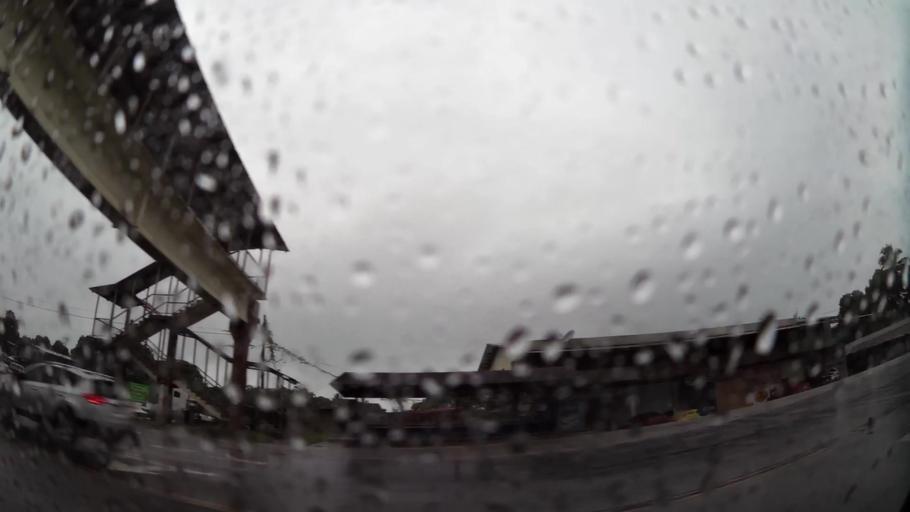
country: PA
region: Colon
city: Santa Rita Arriba
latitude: 9.3327
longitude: -79.8039
